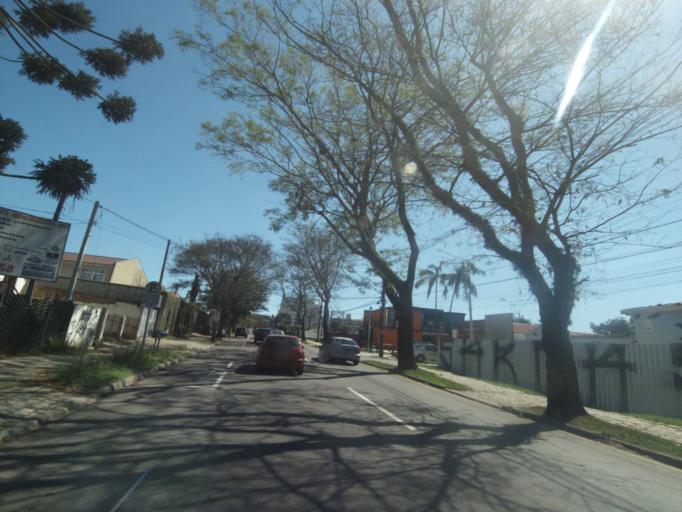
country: BR
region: Parana
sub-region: Curitiba
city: Curitiba
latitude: -25.3976
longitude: -49.2362
